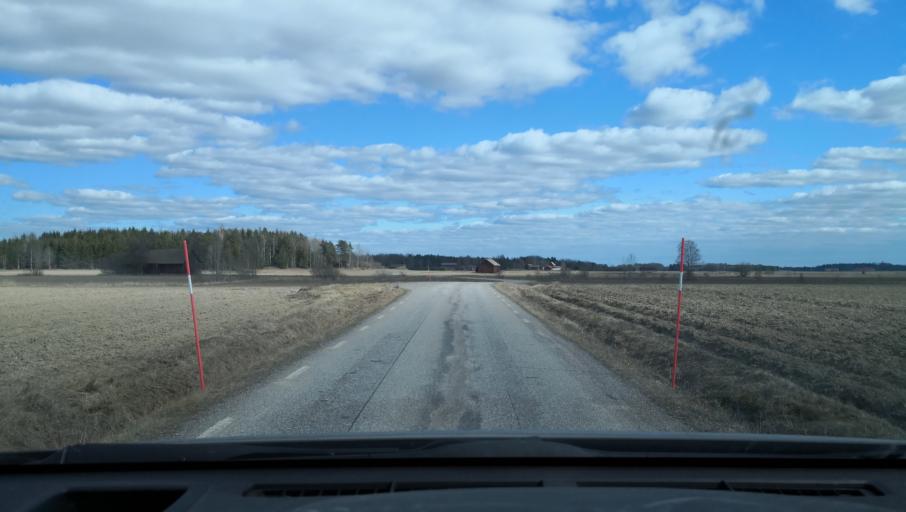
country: SE
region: Vaestmanland
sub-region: Sala Kommun
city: Sala
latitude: 59.8617
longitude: 16.5797
